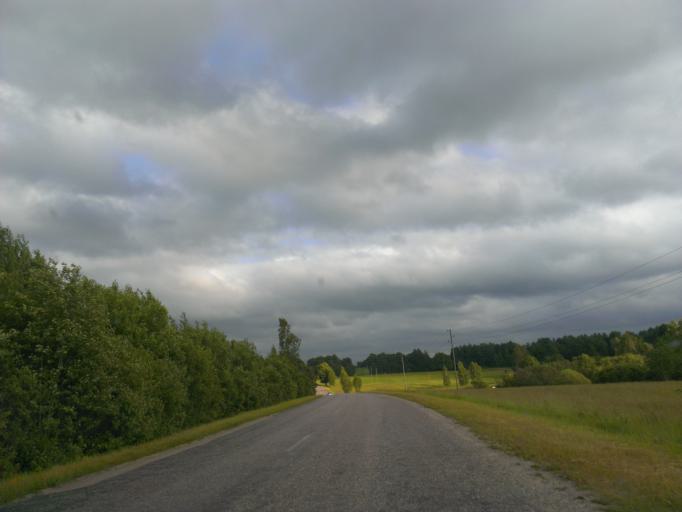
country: LV
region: Aizpute
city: Aizpute
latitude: 56.7130
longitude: 21.7628
